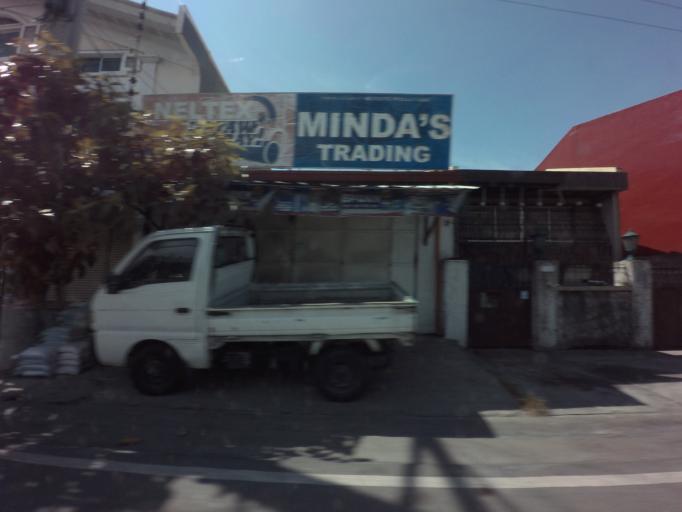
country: PH
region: Calabarzon
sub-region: Province of Rizal
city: Las Pinas
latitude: 14.4423
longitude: 120.9863
